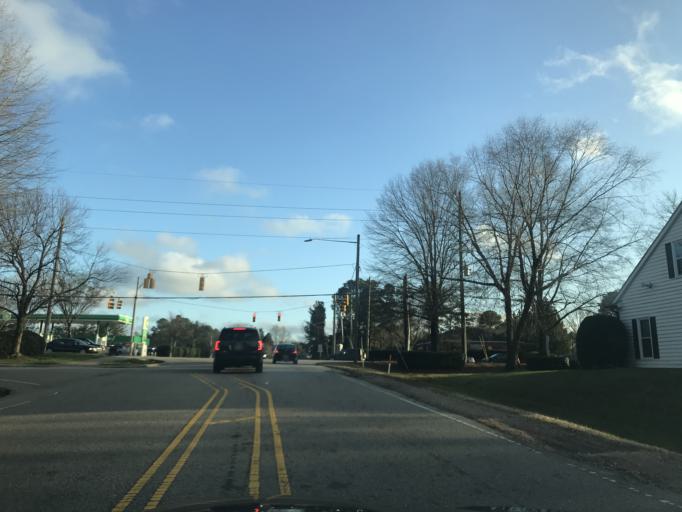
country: US
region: North Carolina
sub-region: Wake County
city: Wake Forest
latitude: 35.9502
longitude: -78.5315
